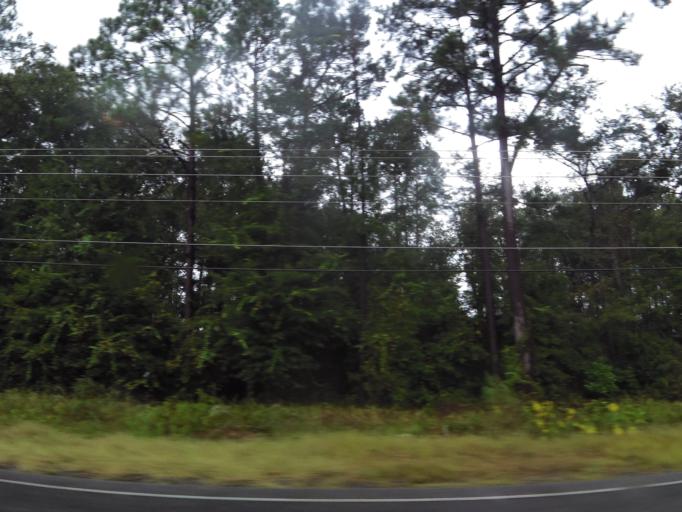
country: US
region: Georgia
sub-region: Wayne County
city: Jesup
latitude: 31.5835
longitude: -81.8774
